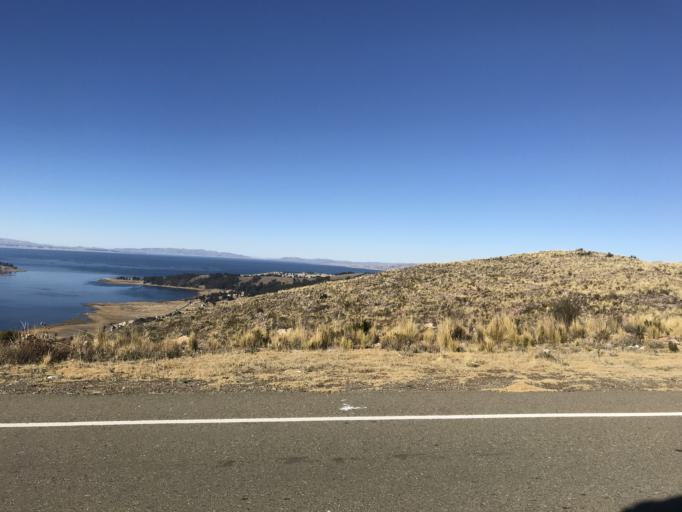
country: BO
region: La Paz
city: San Pedro
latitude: -16.1873
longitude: -68.9629
